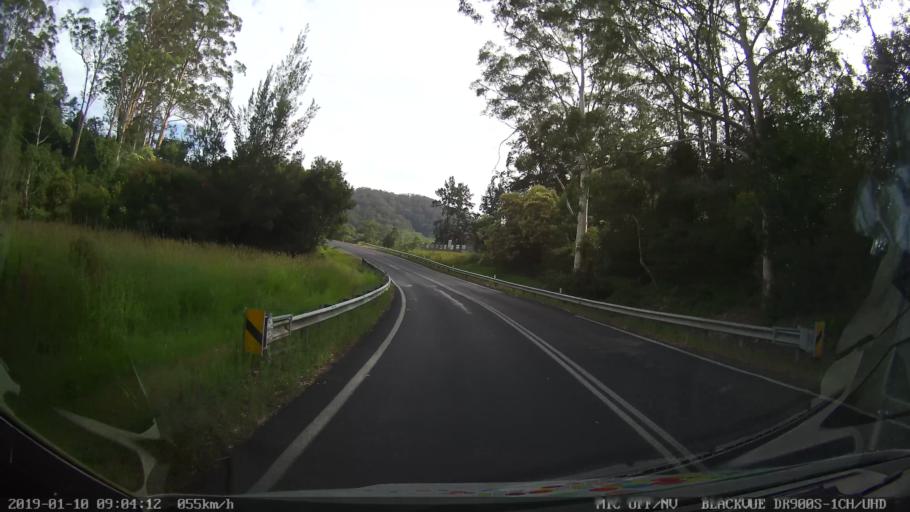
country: AU
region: New South Wales
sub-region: Coffs Harbour
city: Coffs Harbour
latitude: -30.2582
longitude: 153.0521
